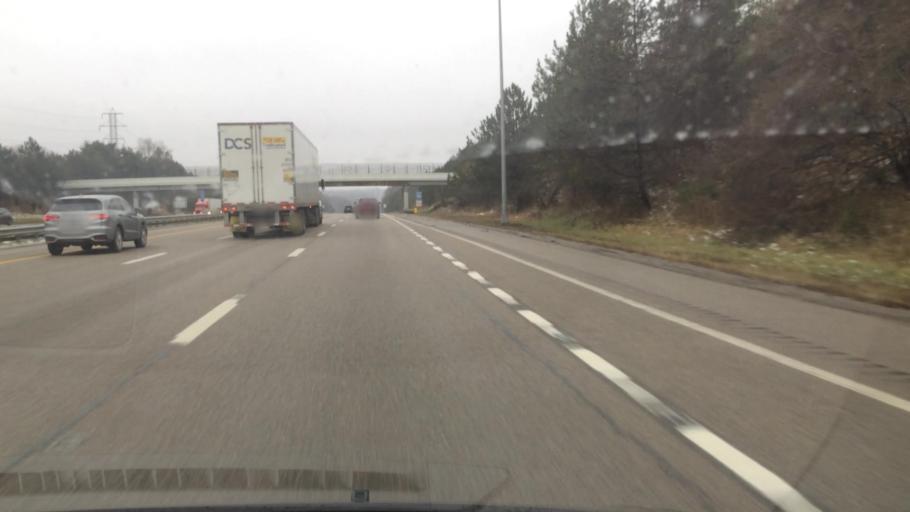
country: US
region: Ohio
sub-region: Cuyahoga County
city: Brecksville
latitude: 41.3386
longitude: -81.6498
